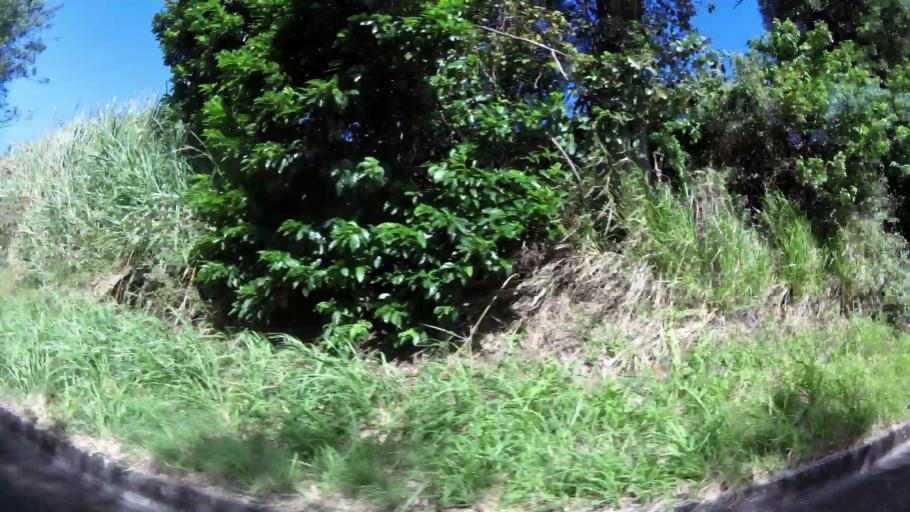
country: MQ
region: Martinique
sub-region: Martinique
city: Le Lorrain
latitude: 14.8356
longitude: -61.0698
